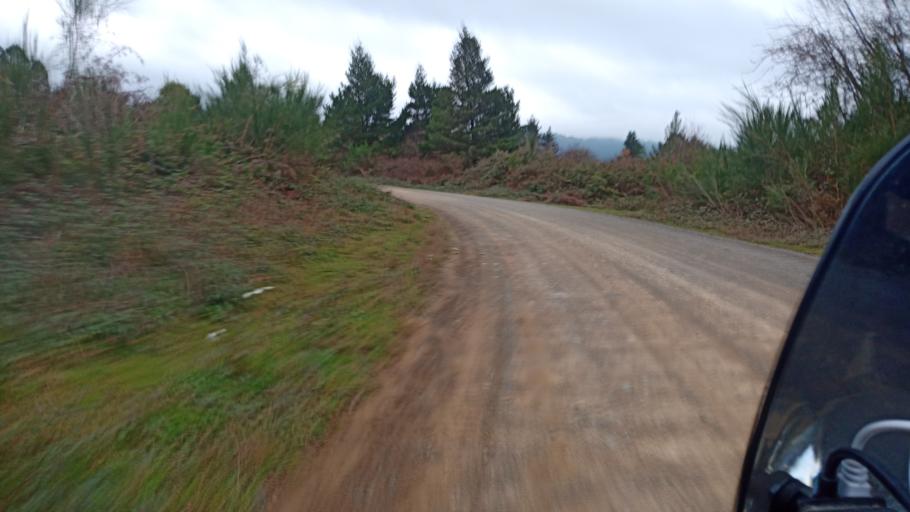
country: NZ
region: Bay of Plenty
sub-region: Whakatane District
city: Murupara
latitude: -38.6382
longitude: 176.7204
